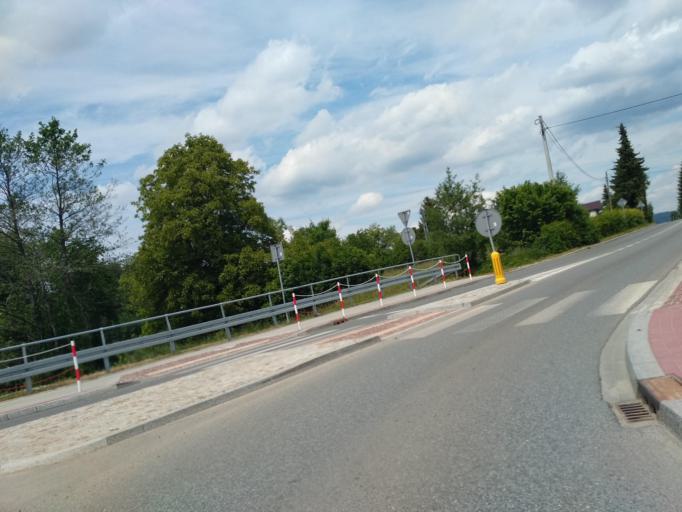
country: PL
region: Subcarpathian Voivodeship
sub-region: Powiat krosnienski
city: Odrzykon
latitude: 49.7049
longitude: 21.7246
